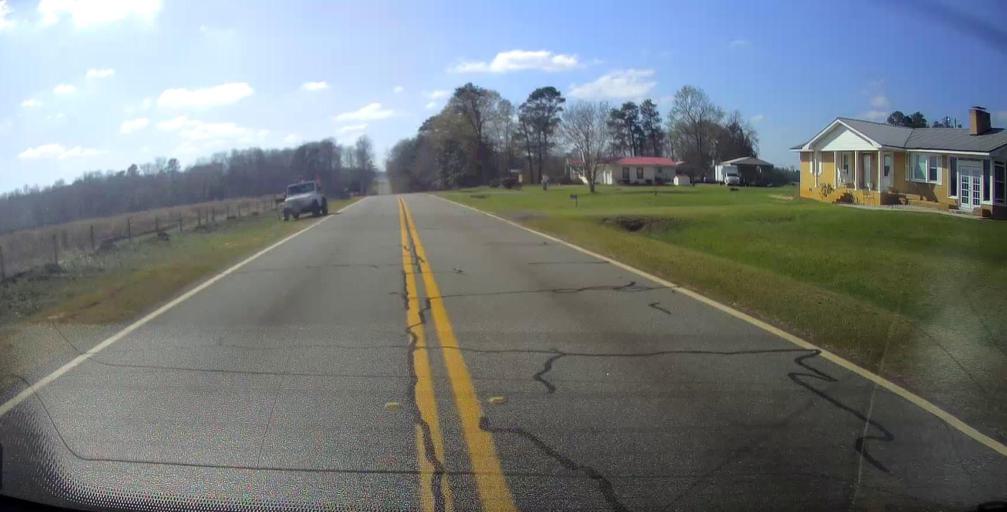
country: US
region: Georgia
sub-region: Twiggs County
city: Jeffersonville
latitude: 32.6813
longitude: -83.2961
